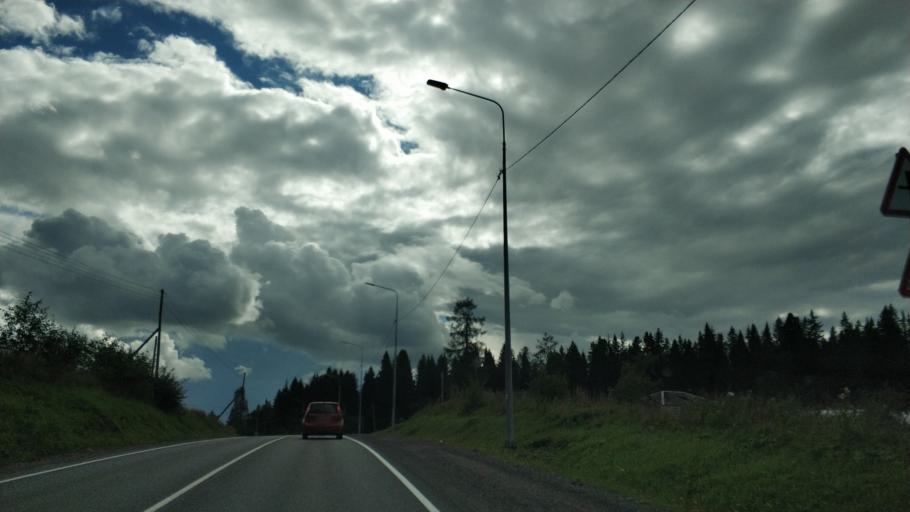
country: RU
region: Republic of Karelia
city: Khelyulya
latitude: 61.7690
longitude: 30.6544
